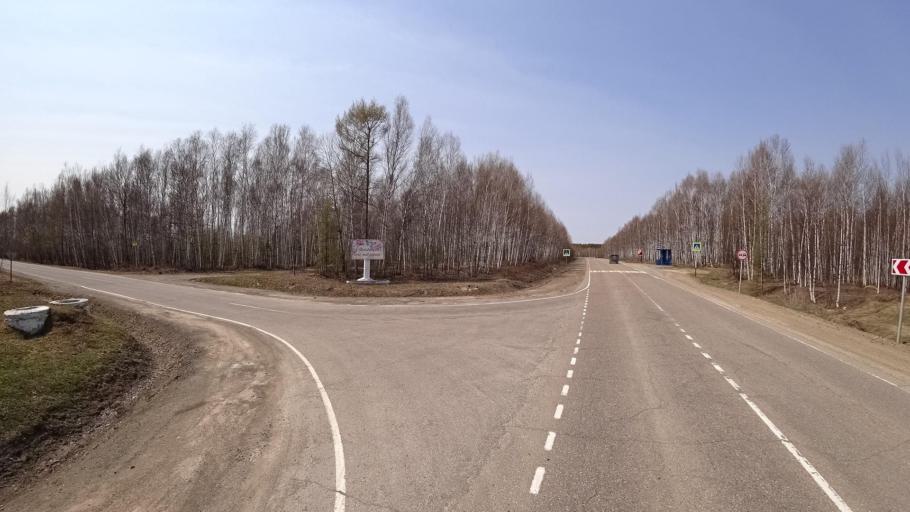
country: RU
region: Khabarovsk Krai
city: Selikhino
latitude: 50.3960
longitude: 137.3735
